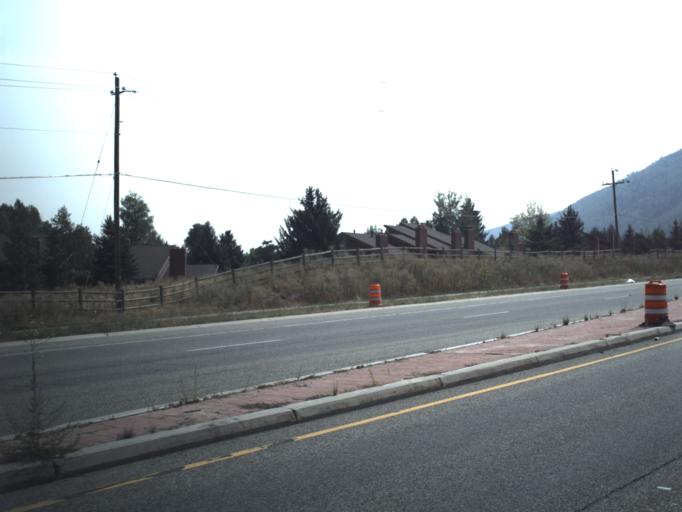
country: US
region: Utah
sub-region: Summit County
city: Snyderville
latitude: 40.6898
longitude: -111.5443
